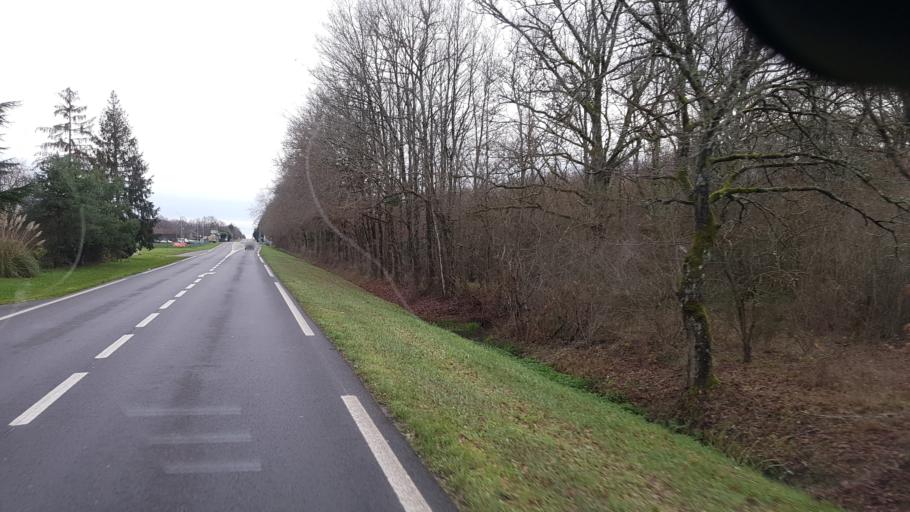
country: FR
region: Centre
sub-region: Departement du Loiret
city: Menestreau-en-Villette
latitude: 47.6551
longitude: 1.9854
